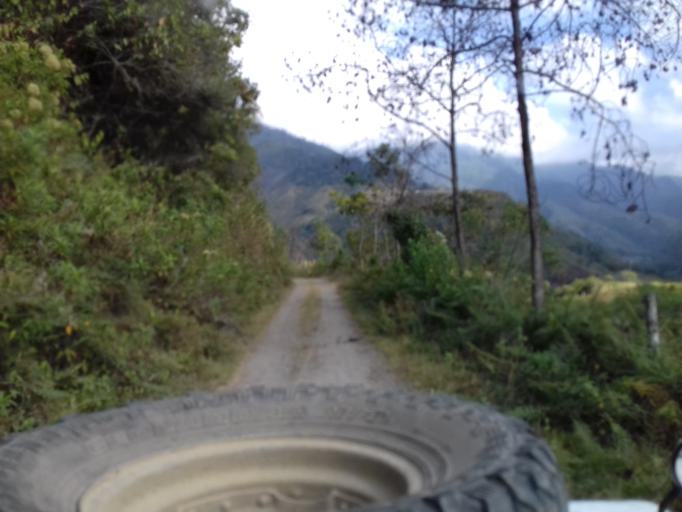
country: CO
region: Tolima
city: Cajamarca
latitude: 4.5293
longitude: -75.4129
